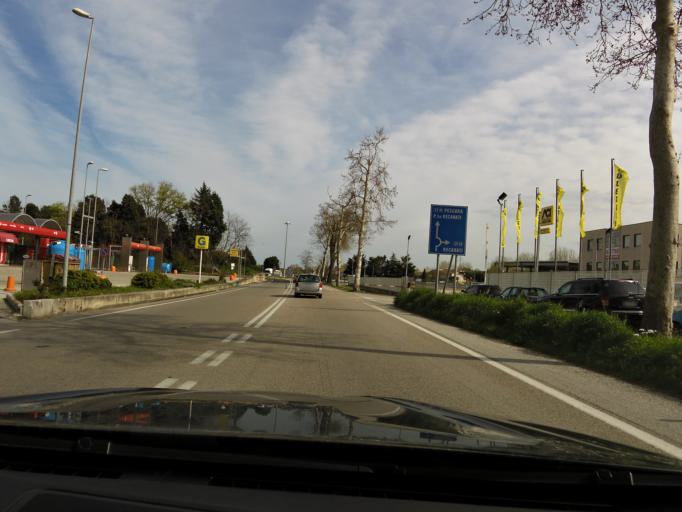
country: IT
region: The Marches
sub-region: Provincia di Macerata
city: Porto Recanati
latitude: 43.4366
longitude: 13.6436
